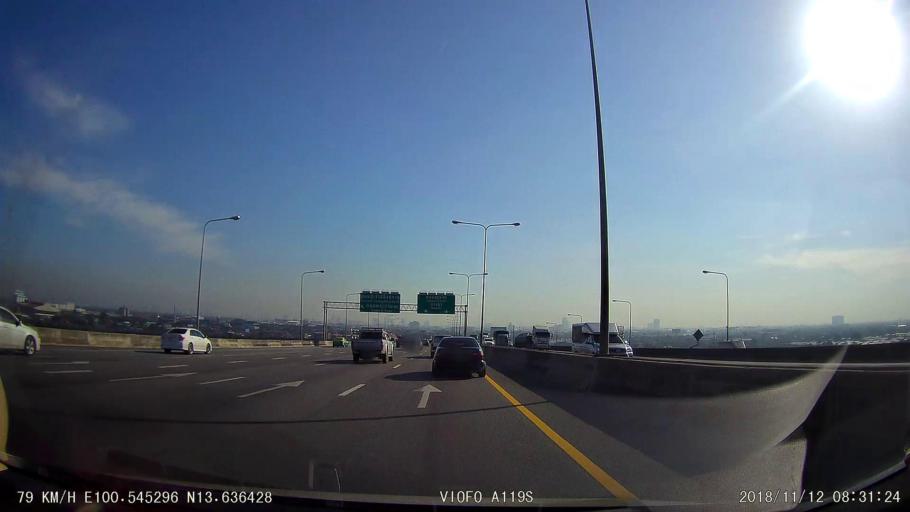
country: TH
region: Samut Prakan
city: Phra Pradaeng
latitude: 13.6366
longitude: 100.5456
